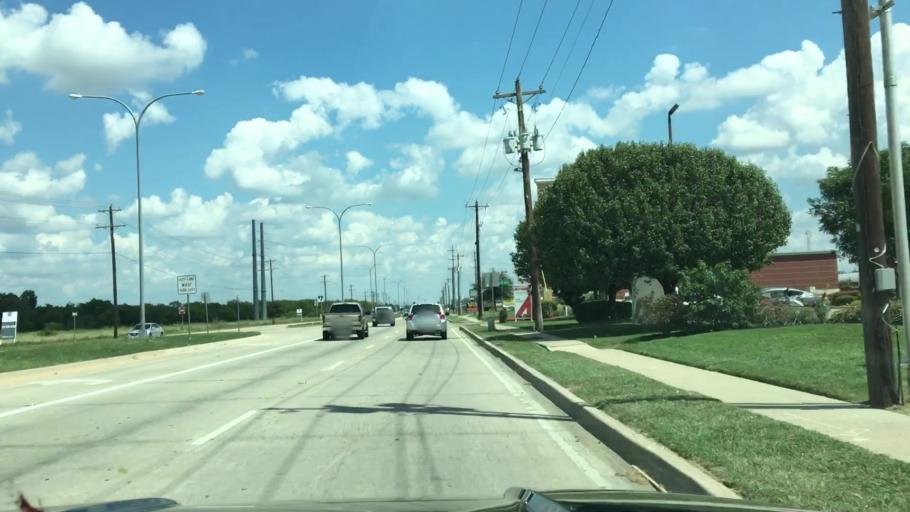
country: US
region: Texas
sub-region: Tarrant County
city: Keller
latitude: 32.9314
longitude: -97.2876
